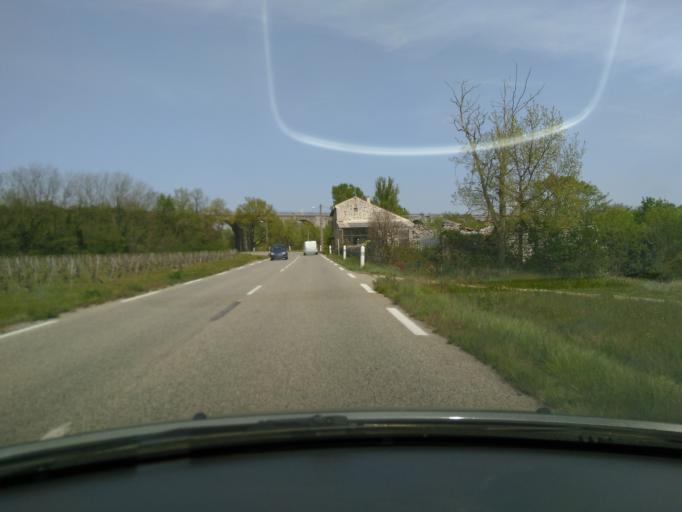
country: FR
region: Rhone-Alpes
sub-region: Departement de l'Ardeche
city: Lavilledieu
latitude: 44.5619
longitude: 4.4602
